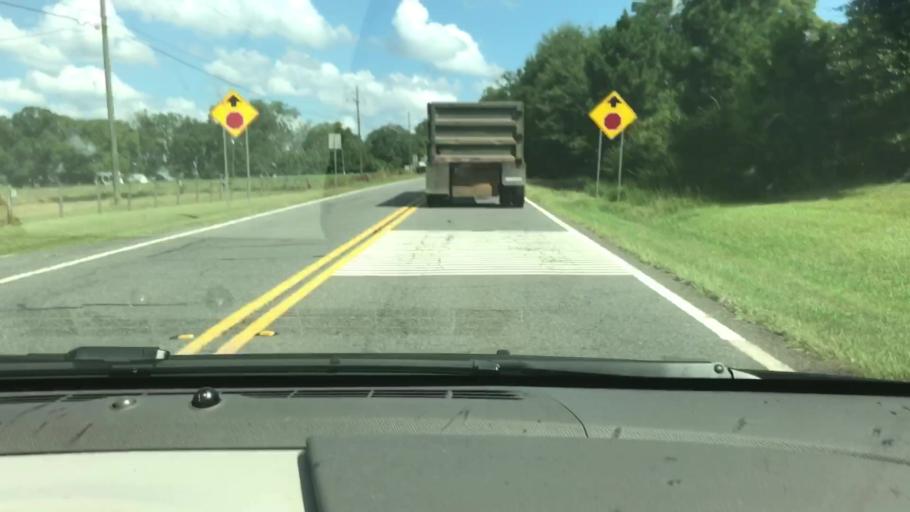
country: US
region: Georgia
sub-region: Troup County
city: West Point
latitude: 32.8675
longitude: -85.0351
